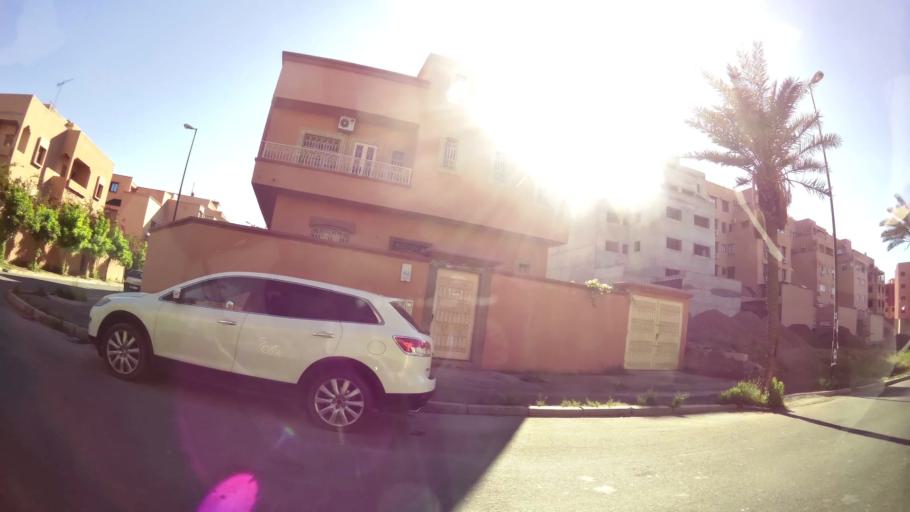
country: MA
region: Marrakech-Tensift-Al Haouz
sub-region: Marrakech
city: Marrakesh
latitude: 31.6461
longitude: -8.0134
